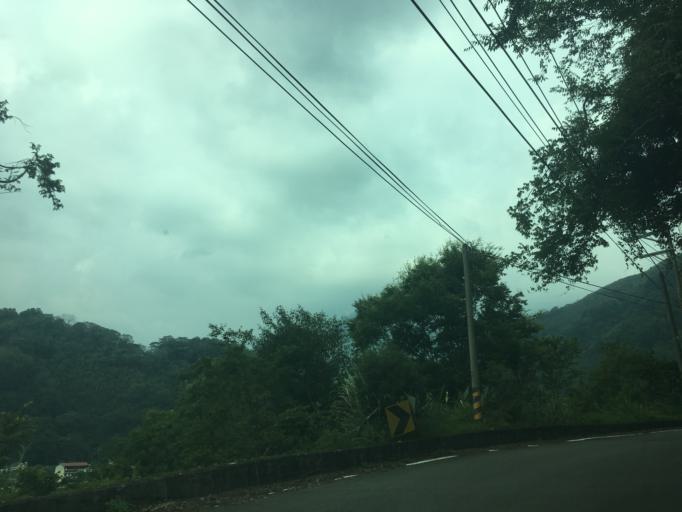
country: TW
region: Taiwan
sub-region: Miaoli
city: Miaoli
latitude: 24.3567
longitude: 120.9471
